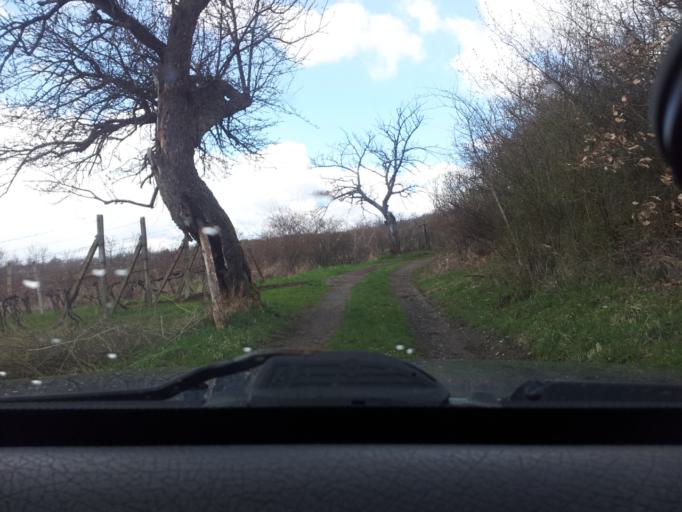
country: SK
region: Nitriansky
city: Tlmace
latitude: 48.3012
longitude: 18.5657
